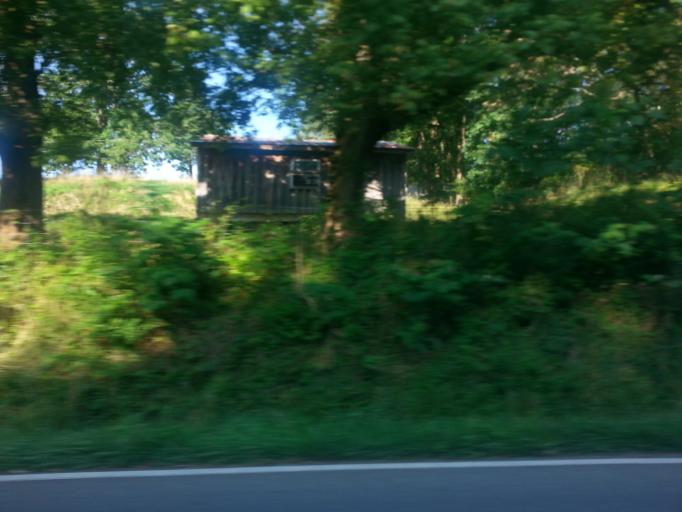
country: US
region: Tennessee
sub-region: Blount County
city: Maryville
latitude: 35.6611
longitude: -83.9617
